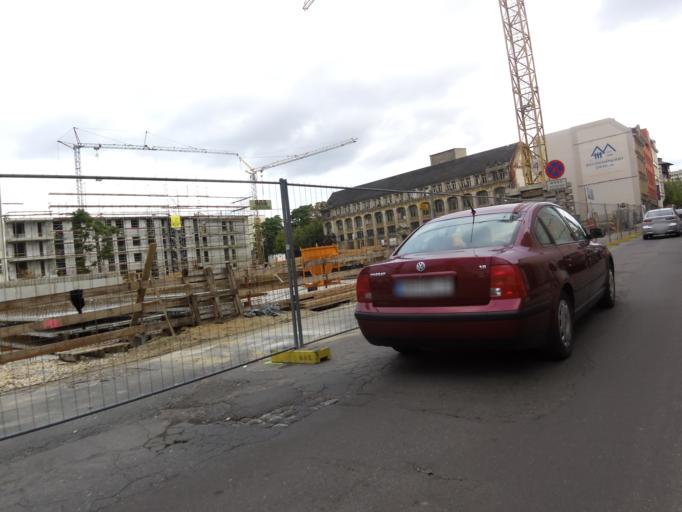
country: DE
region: Saxony
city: Leipzig
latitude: 51.3426
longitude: 12.3850
